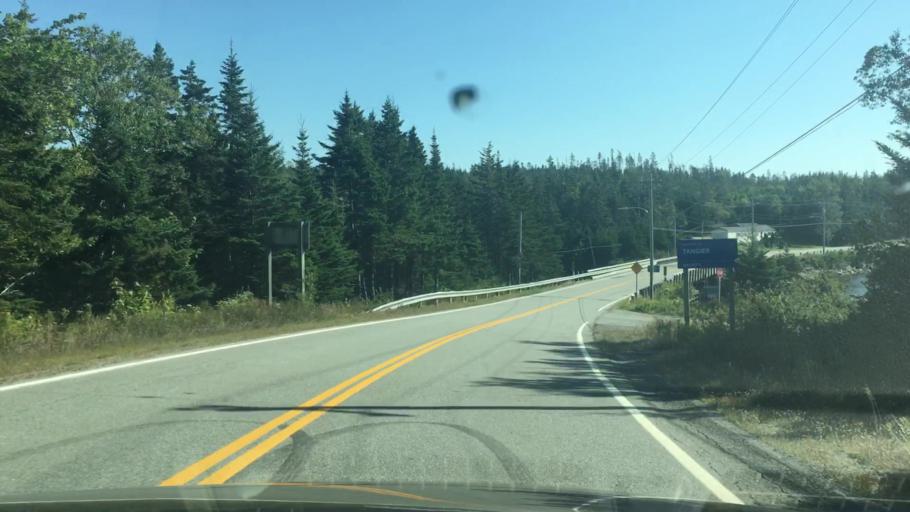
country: CA
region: Nova Scotia
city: Cole Harbour
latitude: 44.8049
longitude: -62.7083
